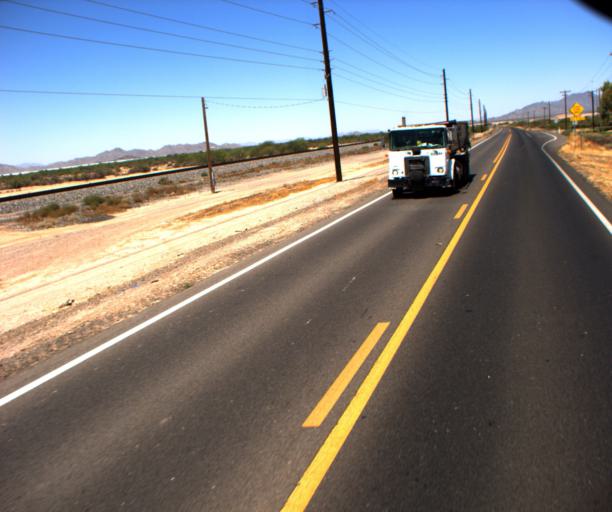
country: US
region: Arizona
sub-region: Pinal County
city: Maricopa
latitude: 33.0751
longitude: -112.0870
